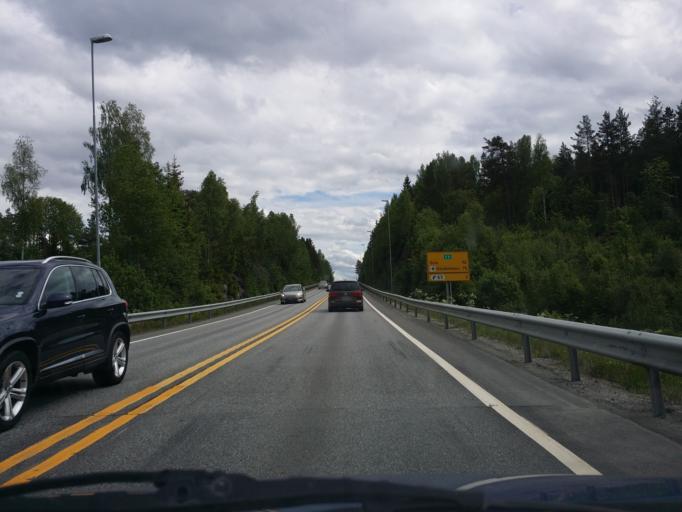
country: NO
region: Hedmark
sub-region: Stange
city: Stange
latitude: 60.7211
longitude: 11.2356
